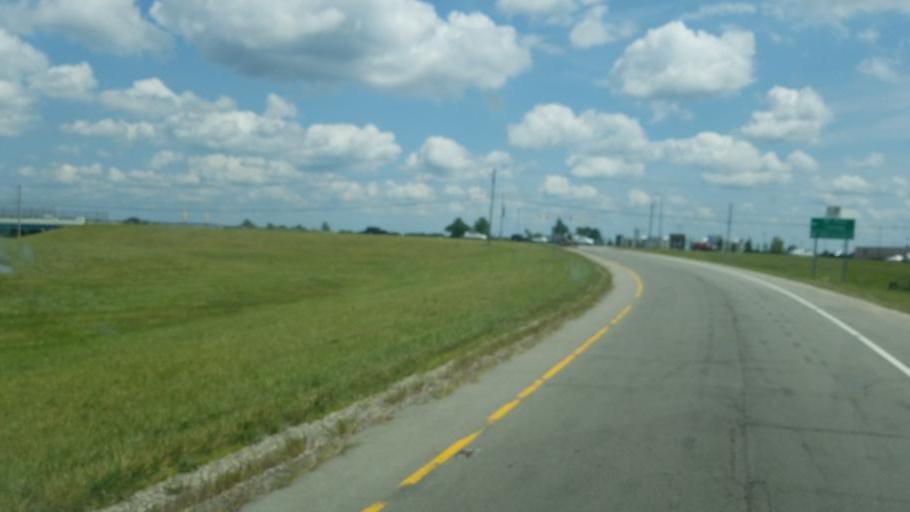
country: US
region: Ohio
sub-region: Richland County
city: Ontario
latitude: 40.7838
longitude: -82.5920
